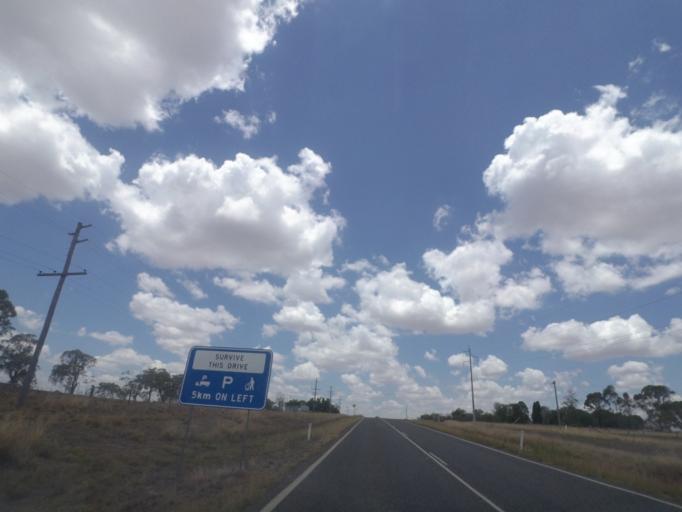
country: AU
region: Queensland
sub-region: Toowoomba
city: Top Camp
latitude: -27.8830
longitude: 151.9705
